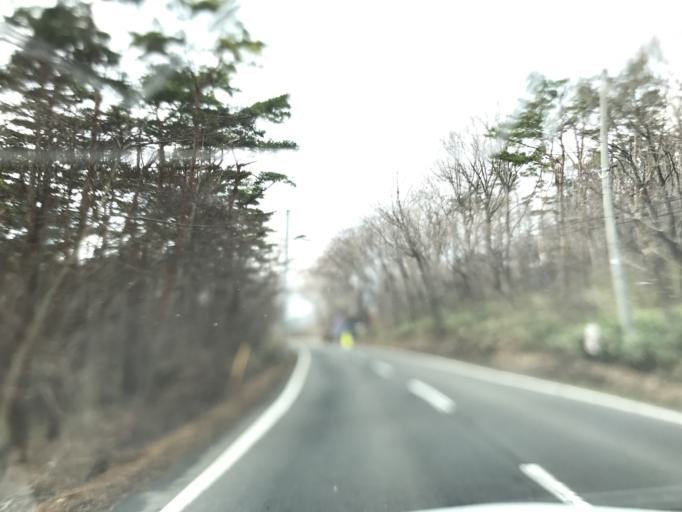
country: JP
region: Miyagi
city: Shiroishi
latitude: 38.0396
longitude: 140.5318
